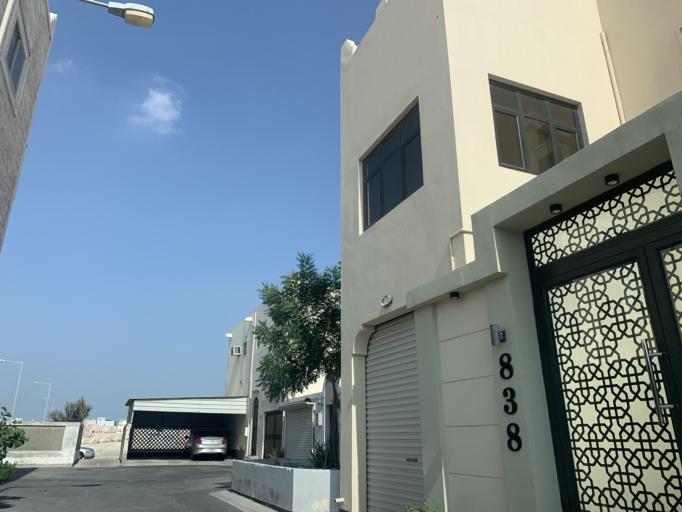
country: BH
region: Central Governorate
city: Madinat Hamad
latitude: 26.1389
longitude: 50.5008
